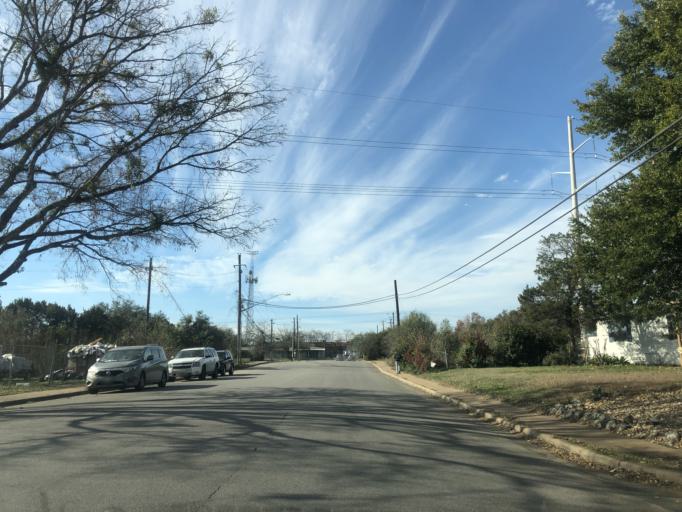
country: US
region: Texas
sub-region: Travis County
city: Onion Creek
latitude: 30.1830
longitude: -97.7672
